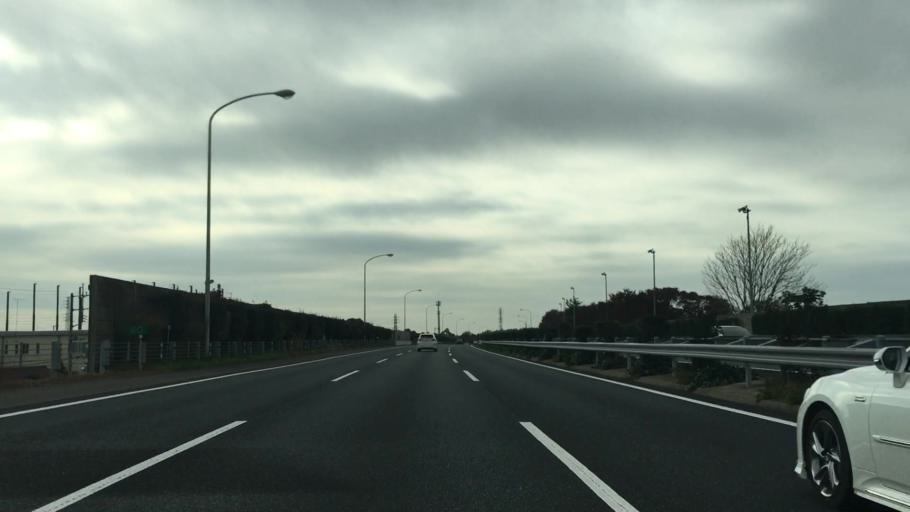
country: JP
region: Chiba
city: Narita
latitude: 35.7472
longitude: 140.3144
